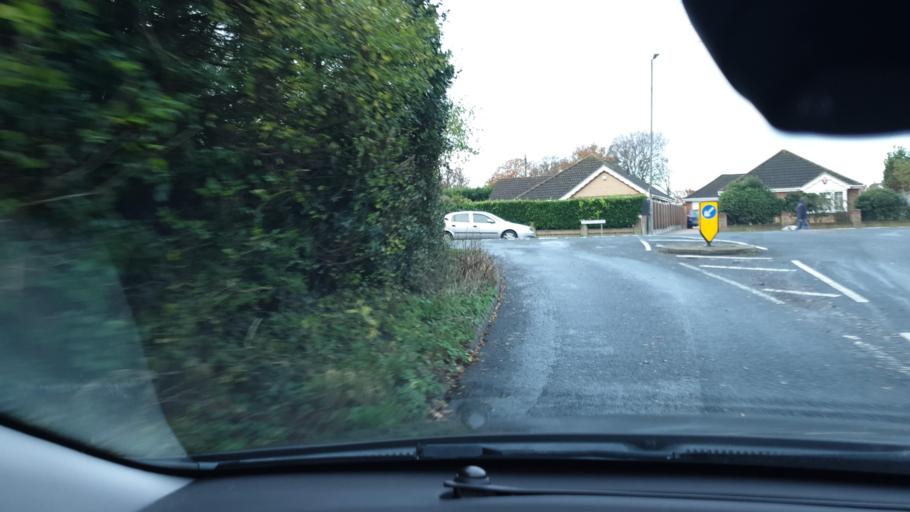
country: GB
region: England
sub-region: Essex
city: Clacton-on-Sea
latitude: 51.7888
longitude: 1.1202
